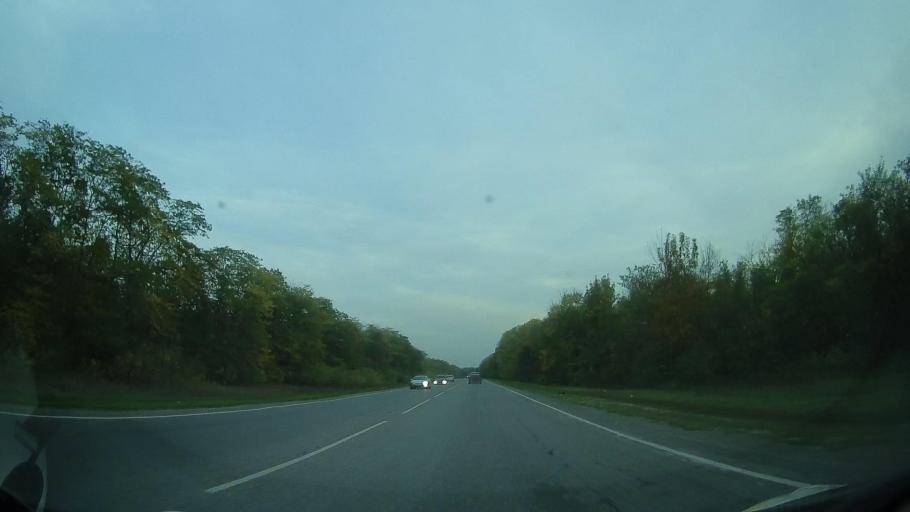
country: RU
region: Rostov
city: Kirovskaya
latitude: 46.9951
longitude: 40.0112
